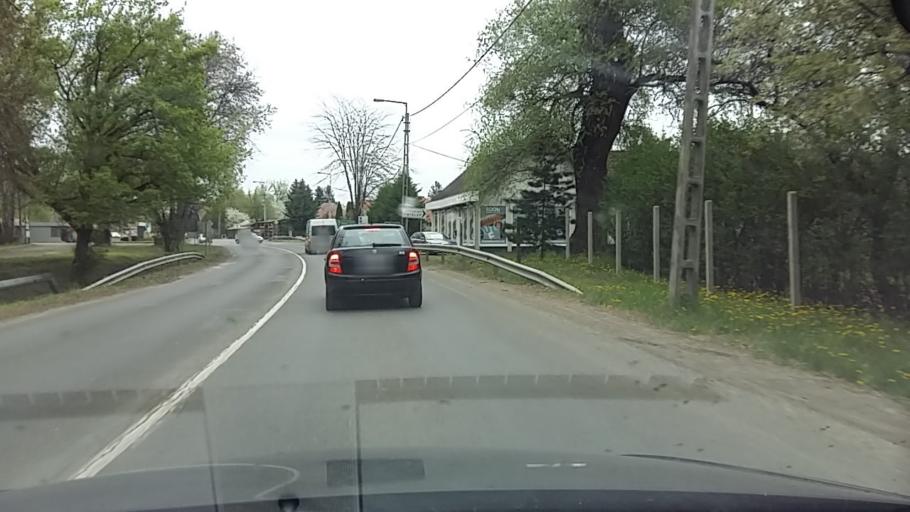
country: HU
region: Pest
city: Szodliget
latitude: 47.7315
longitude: 19.1385
